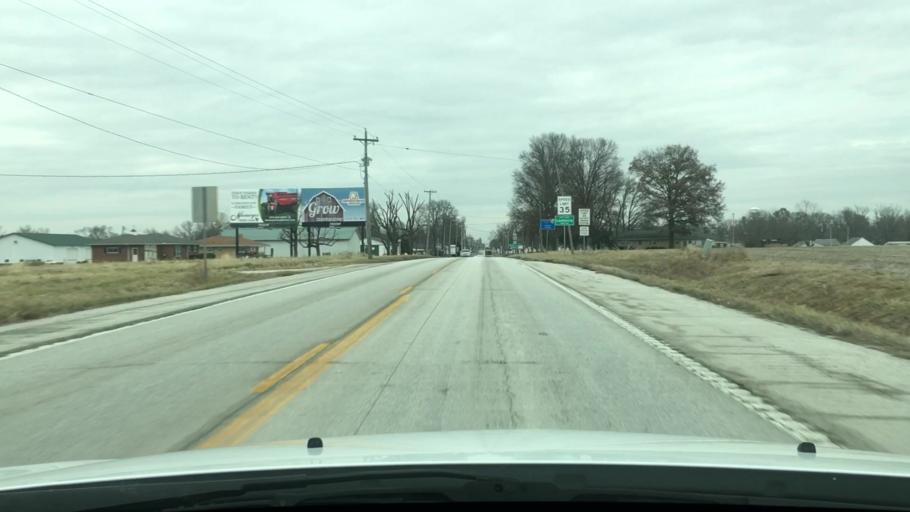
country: US
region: Missouri
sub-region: Audrain County
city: Vandalia
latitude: 39.2341
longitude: -91.6458
